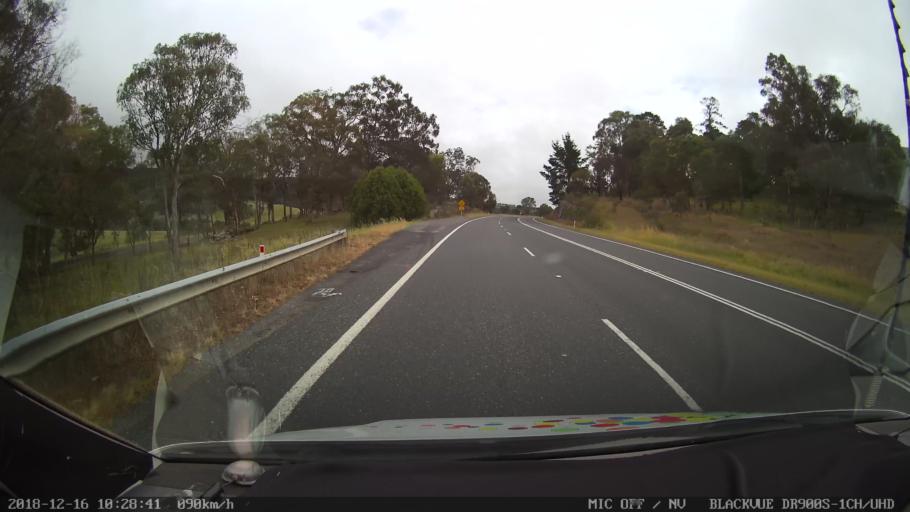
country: AU
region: New South Wales
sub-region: Tenterfield Municipality
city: Carrolls Creek
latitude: -29.1180
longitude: 151.9964
